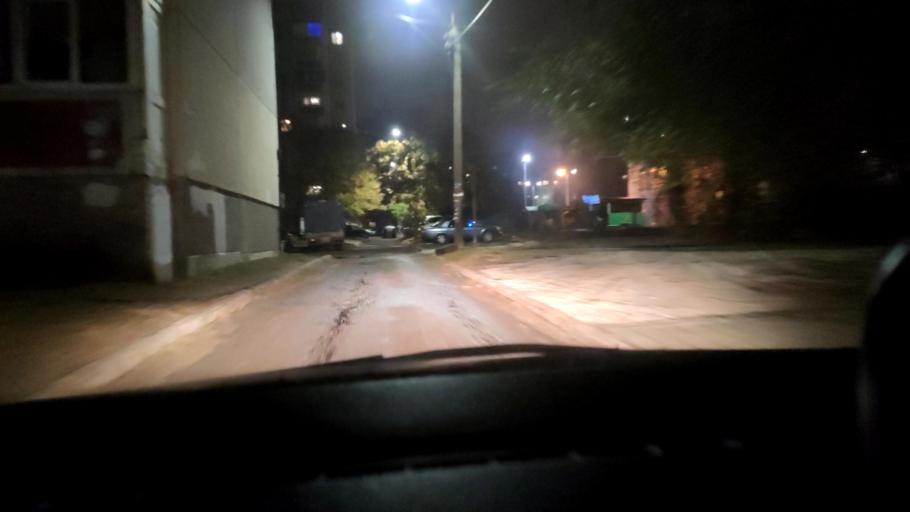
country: RU
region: Voronezj
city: Podgornoye
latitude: 51.6989
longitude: 39.1383
